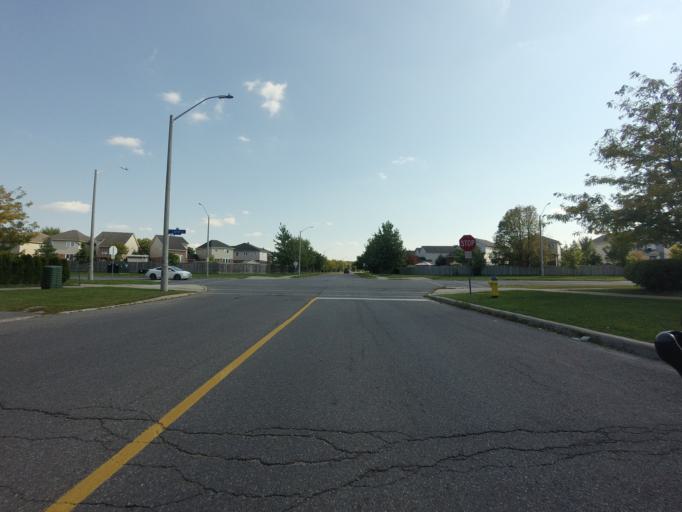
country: CA
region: Ontario
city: Ottawa
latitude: 45.2851
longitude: -75.6807
